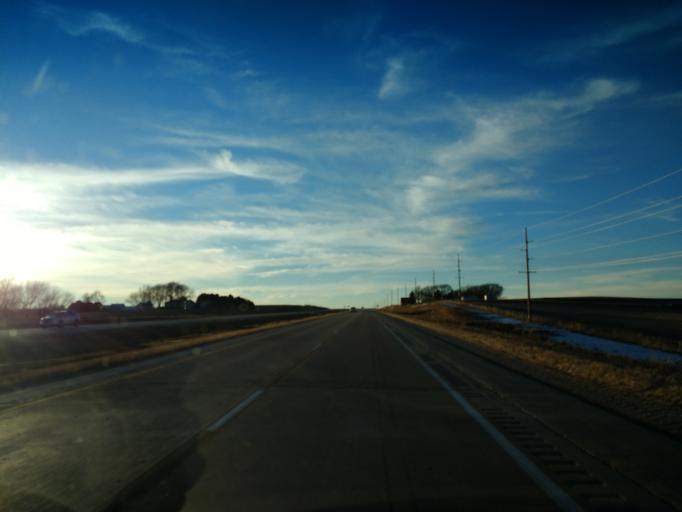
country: US
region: Iowa
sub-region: Ida County
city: Holstein
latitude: 42.4751
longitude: -95.4727
